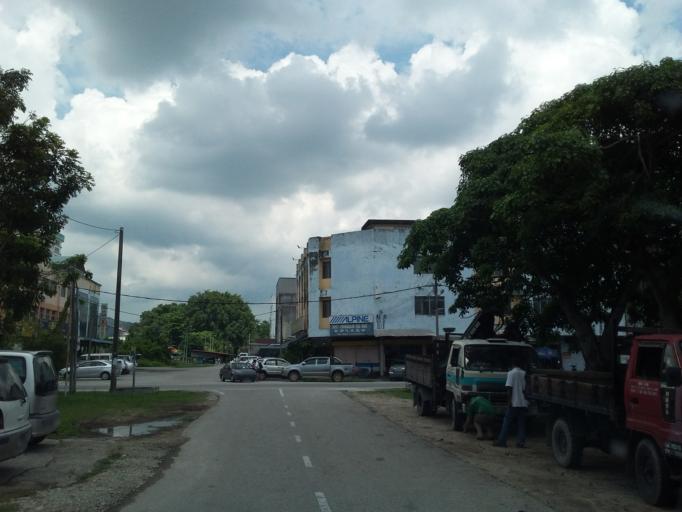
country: MY
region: Johor
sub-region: Daerah Batu Pahat
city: Batu Pahat
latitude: 1.8561
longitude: 102.9257
